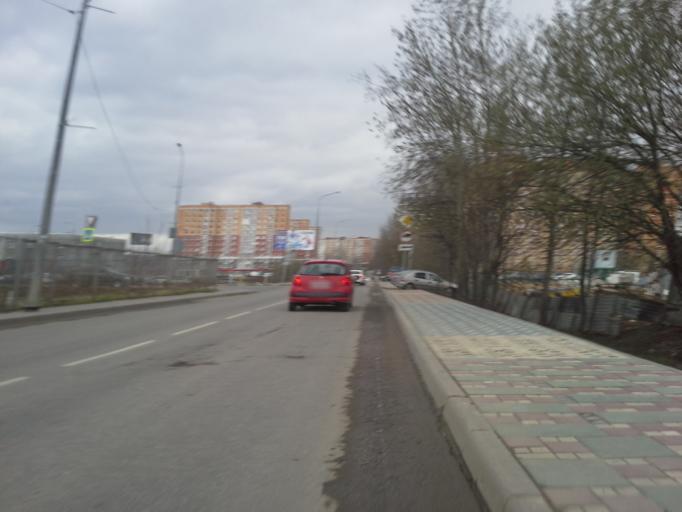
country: RU
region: Moskovskaya
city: Kommunarka
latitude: 55.5759
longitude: 37.4810
